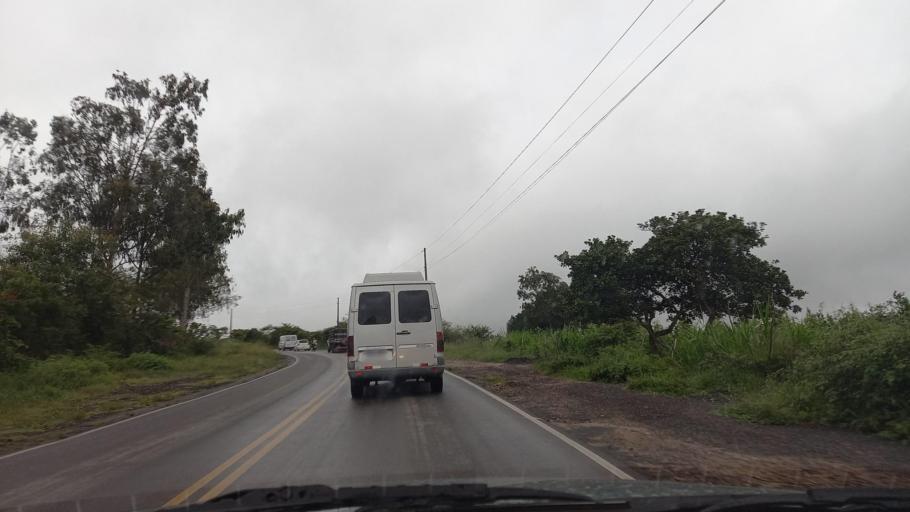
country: BR
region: Pernambuco
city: Garanhuns
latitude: -8.8522
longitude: -36.5152
